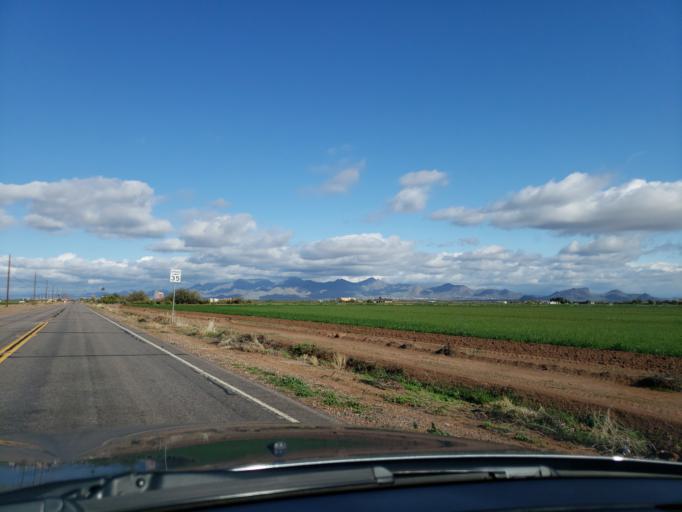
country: US
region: Arizona
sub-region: Maricopa County
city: Scottsdale
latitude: 33.5110
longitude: -111.8740
